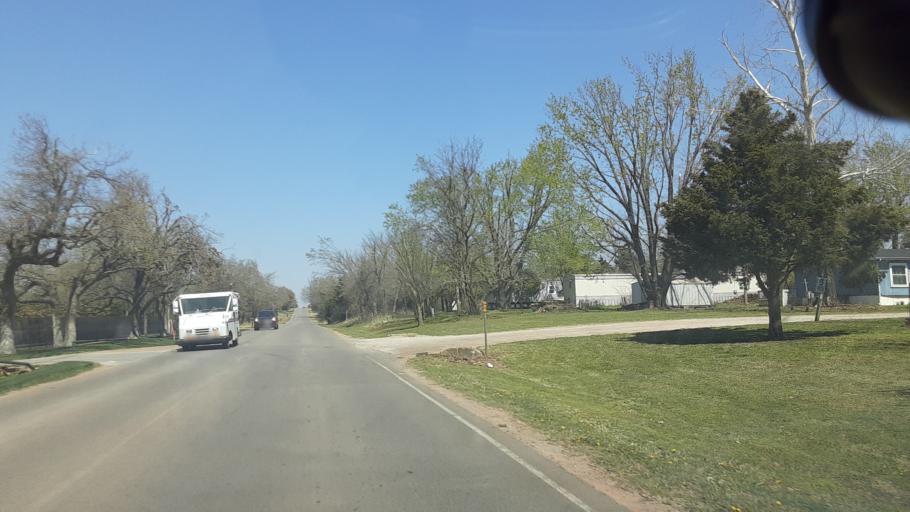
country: US
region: Oklahoma
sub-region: Oklahoma County
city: Edmond
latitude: 35.7600
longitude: -97.4784
